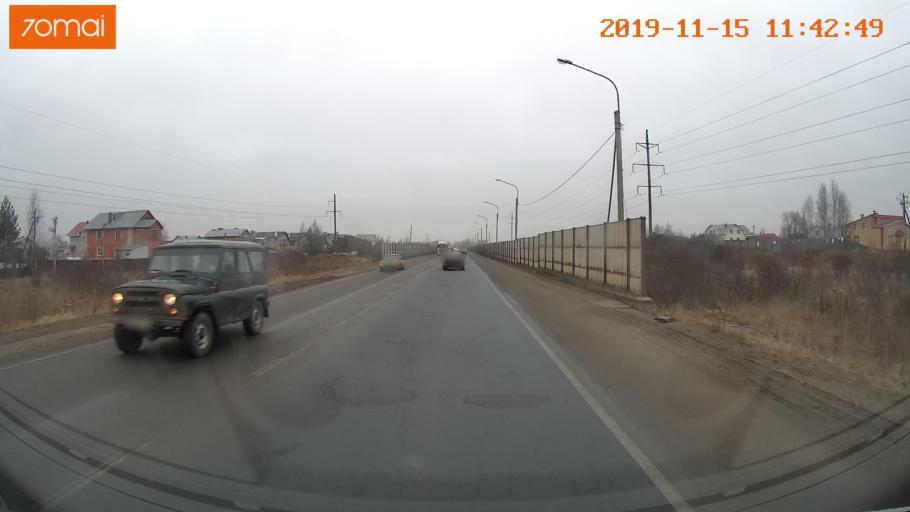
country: RU
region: Vologda
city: Vologda
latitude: 59.2224
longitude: 39.7747
